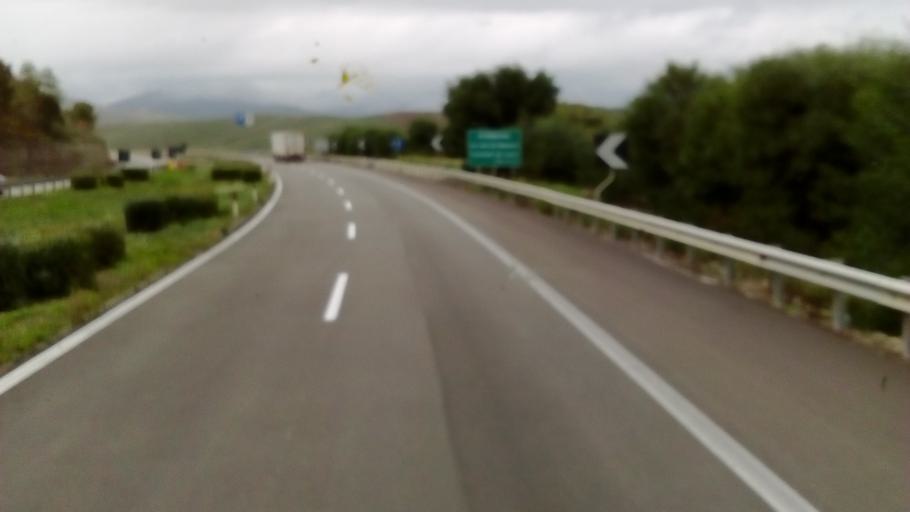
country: IT
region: Sicily
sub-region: Enna
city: Calascibetta
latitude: 37.5793
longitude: 14.2403
